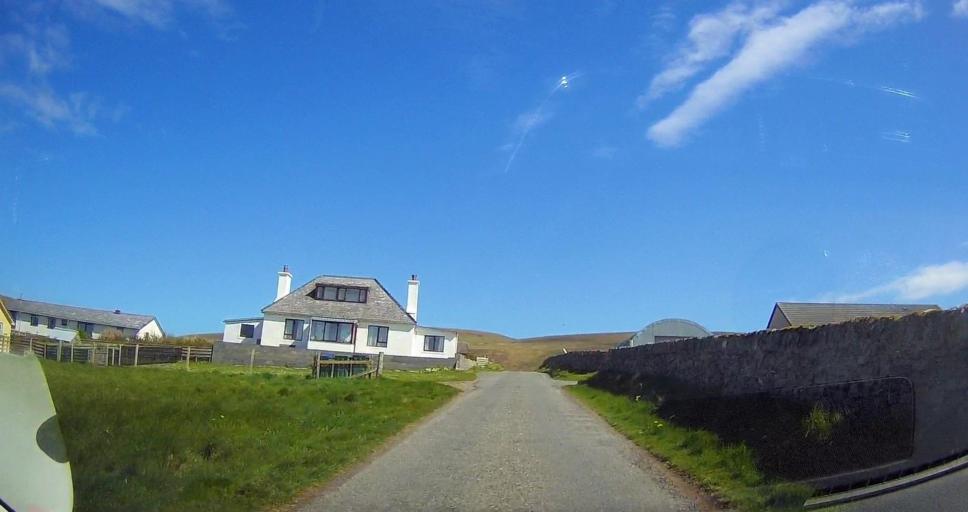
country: GB
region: Scotland
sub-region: Shetland Islands
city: Sandwick
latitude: 59.9730
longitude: -1.3236
